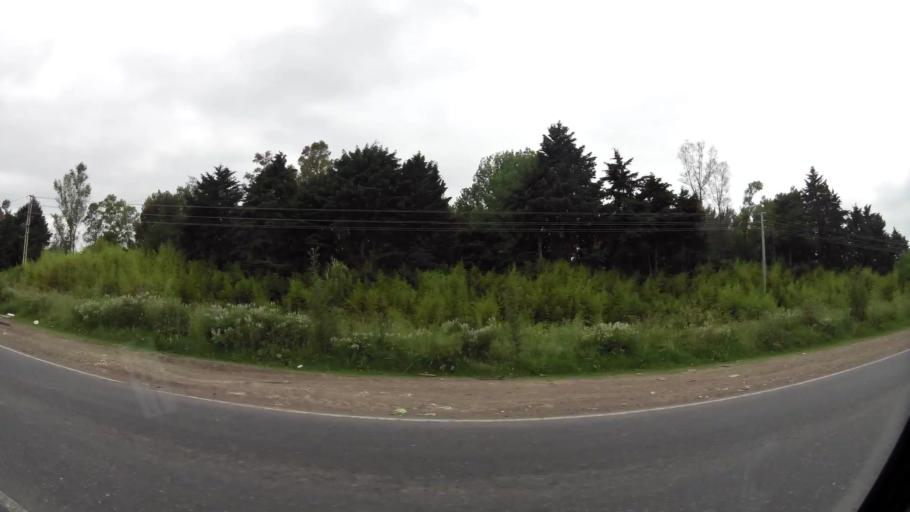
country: AR
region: Buenos Aires
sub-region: Partido de Ezeiza
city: Ezeiza
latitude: -34.8937
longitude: -58.5075
